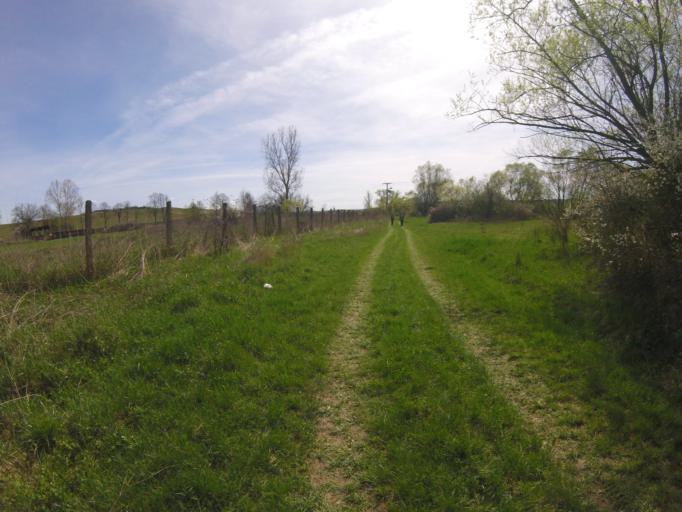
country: HU
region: Borsod-Abauj-Zemplen
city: Szendro
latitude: 48.4188
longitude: 20.7285
